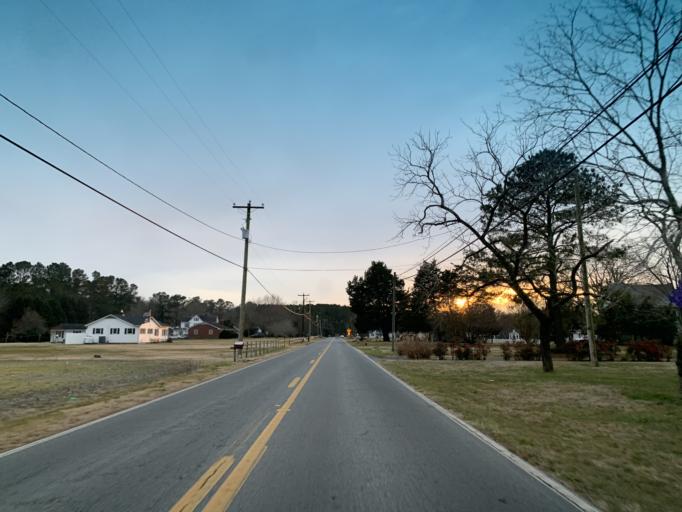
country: US
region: Maryland
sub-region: Worcester County
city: Pocomoke City
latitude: 38.0775
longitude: -75.5483
